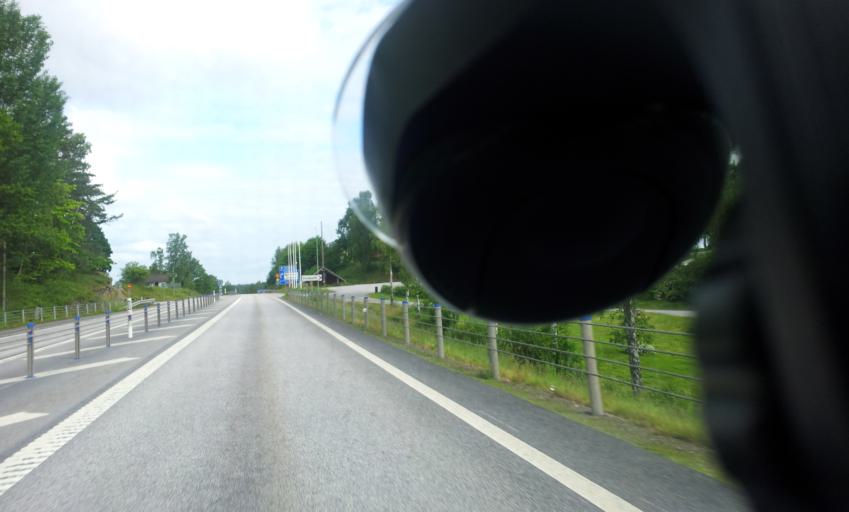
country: SE
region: Kalmar
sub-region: Vasterviks Kommun
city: Gamleby
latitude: 57.8671
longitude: 16.4170
